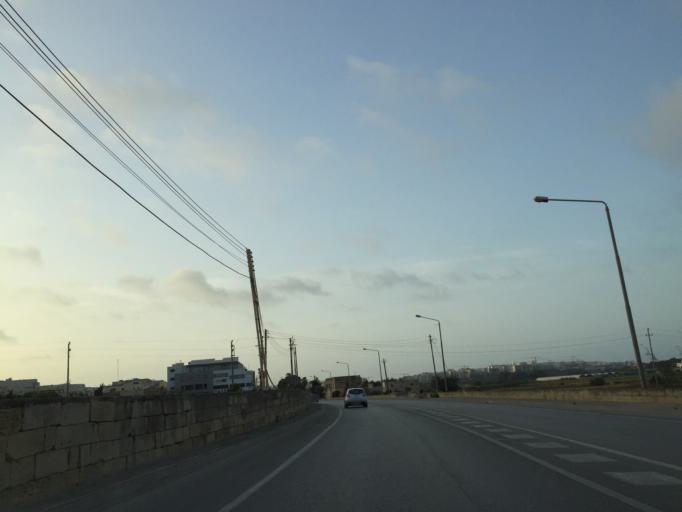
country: MT
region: Saint Paul's Bay
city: San Pawl il-Bahar
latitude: 35.9303
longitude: 14.4164
